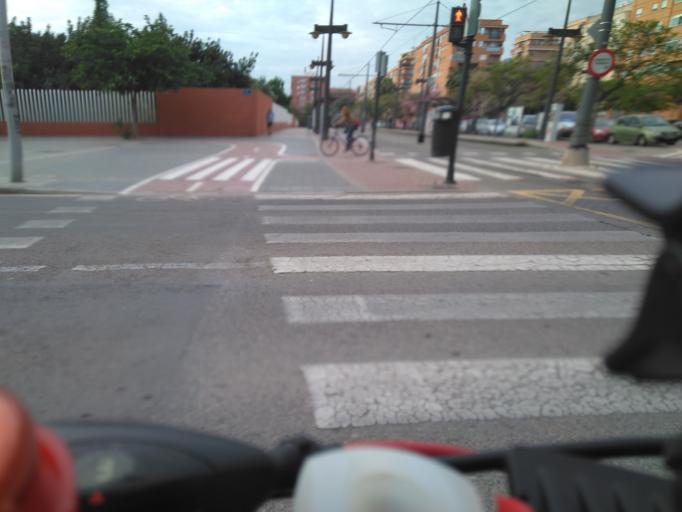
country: ES
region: Valencia
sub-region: Provincia de Valencia
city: Valencia
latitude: 39.4884
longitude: -0.3840
